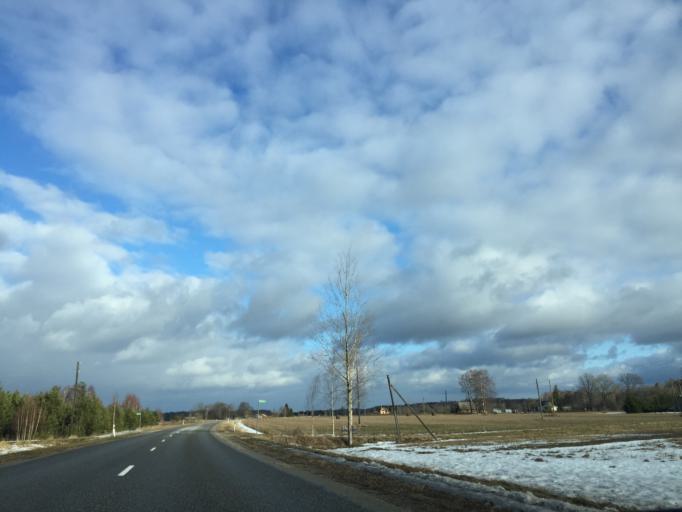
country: LV
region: Salacgrivas
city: Ainazi
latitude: 57.8622
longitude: 24.5416
